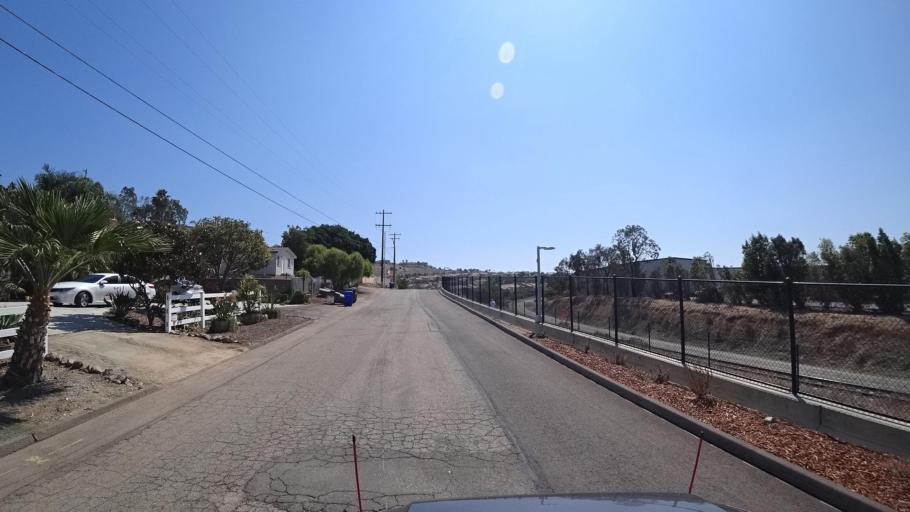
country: US
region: California
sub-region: San Diego County
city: Lake San Marcos
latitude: 33.1648
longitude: -117.2006
